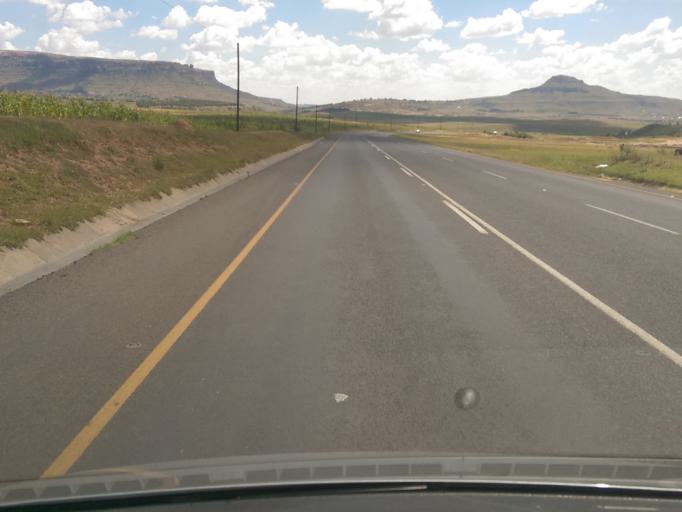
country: LS
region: Maseru
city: Maseru
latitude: -29.3966
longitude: 27.5160
